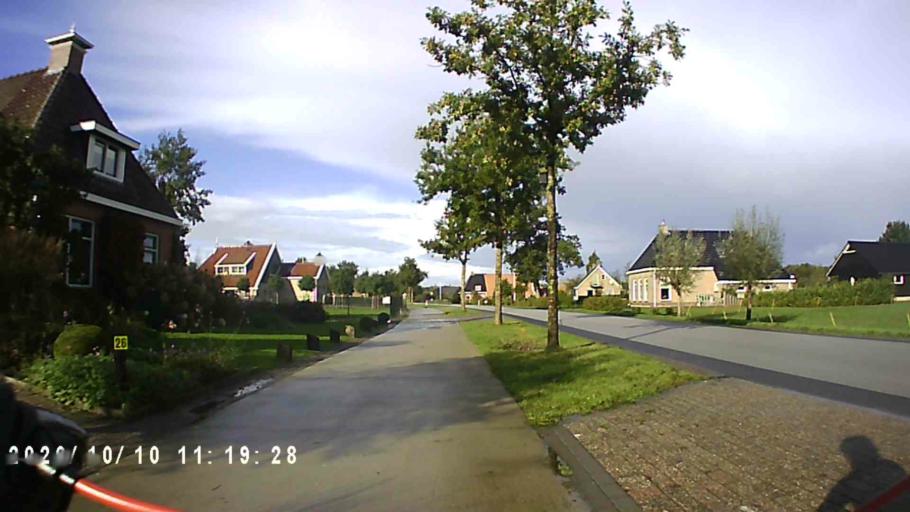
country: NL
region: Friesland
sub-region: Gemeente Smallingerland
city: Drachtstercompagnie
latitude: 53.0949
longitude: 6.1915
